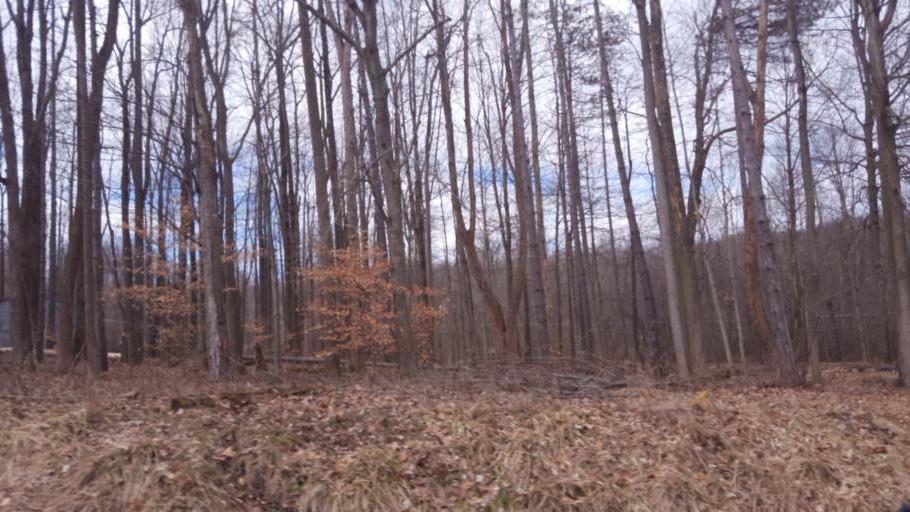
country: US
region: Ohio
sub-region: Sandusky County
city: Bellville
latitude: 40.6709
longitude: -82.5114
